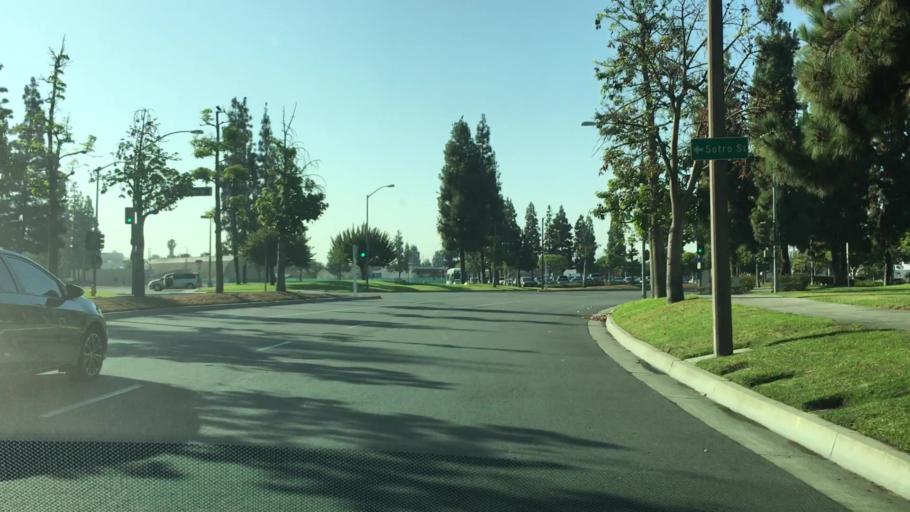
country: US
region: California
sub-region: Los Angeles County
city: La Puente
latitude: 34.0227
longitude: -117.9556
